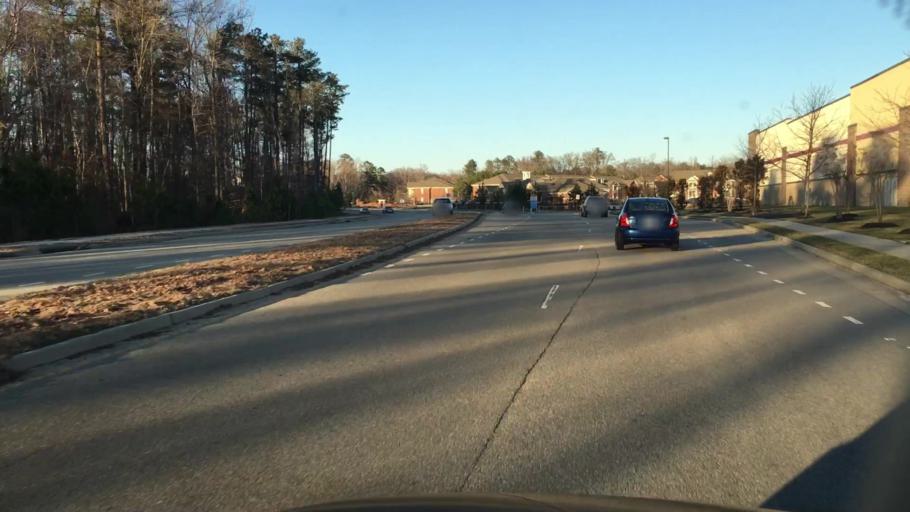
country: US
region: Virginia
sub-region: Chesterfield County
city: Bon Air
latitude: 37.5145
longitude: -77.6062
